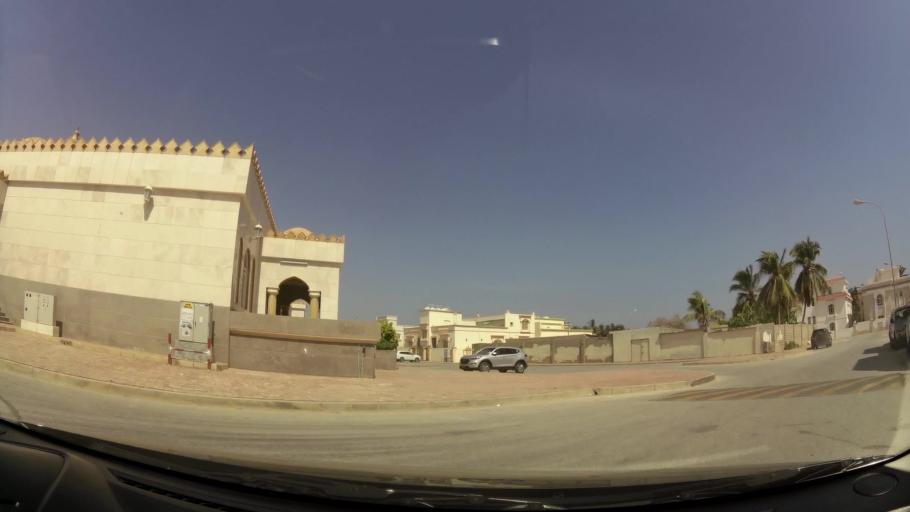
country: OM
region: Zufar
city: Salalah
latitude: 17.0399
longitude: 54.1570
